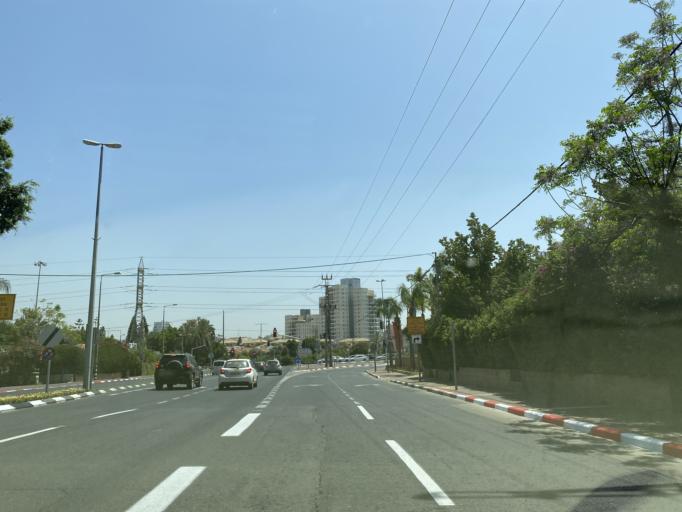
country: IL
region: Central District
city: Ra'anana
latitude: 32.1777
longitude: 34.8871
